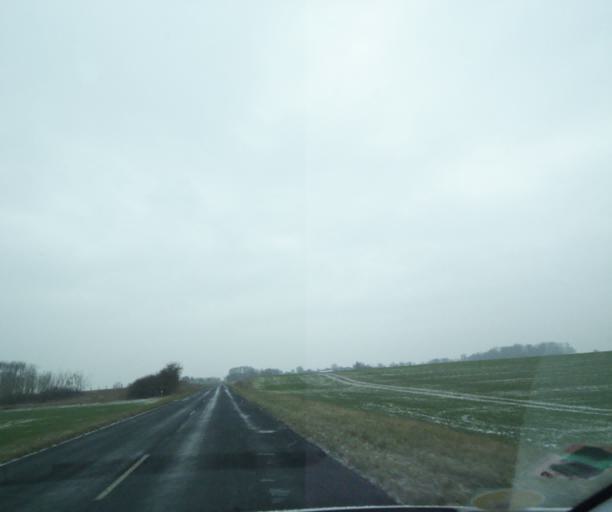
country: FR
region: Champagne-Ardenne
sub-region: Departement de la Haute-Marne
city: Wassy
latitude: 48.4669
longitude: 5.0273
